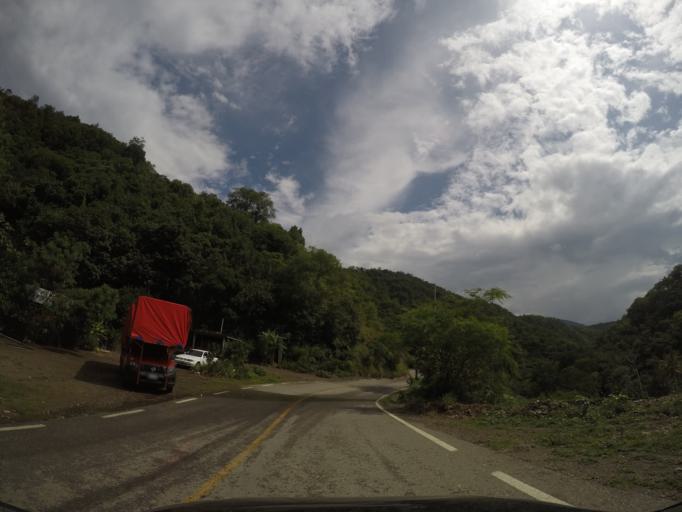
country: MX
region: Oaxaca
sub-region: San Jeronimo Coatlan
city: San Cristobal Honduras
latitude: 16.3748
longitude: -97.0787
